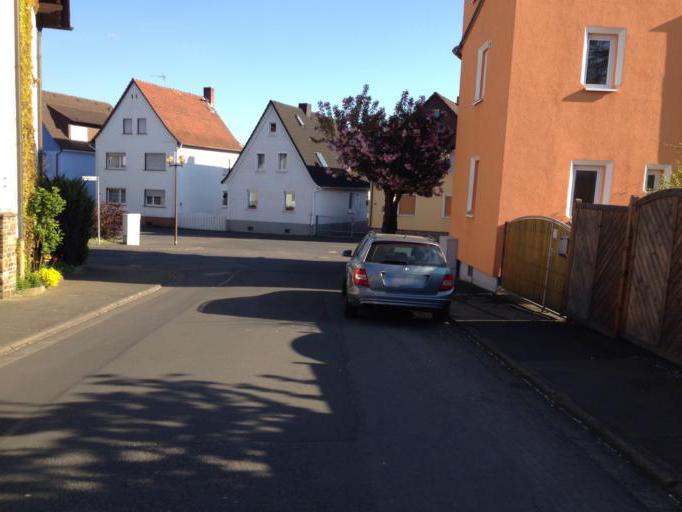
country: DE
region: Hesse
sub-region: Regierungsbezirk Giessen
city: Lich
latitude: 50.5491
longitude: 8.7812
